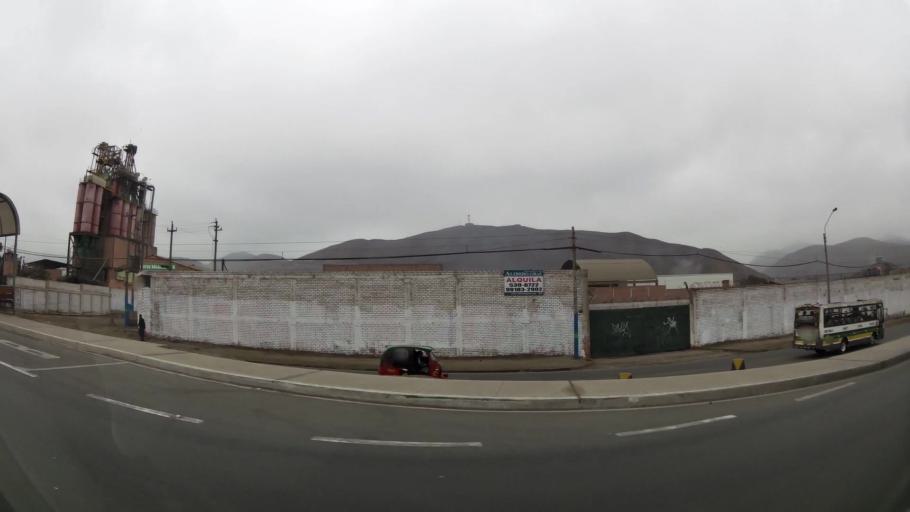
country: PE
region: Lima
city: Ventanilla
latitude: -11.8675
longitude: -77.1282
